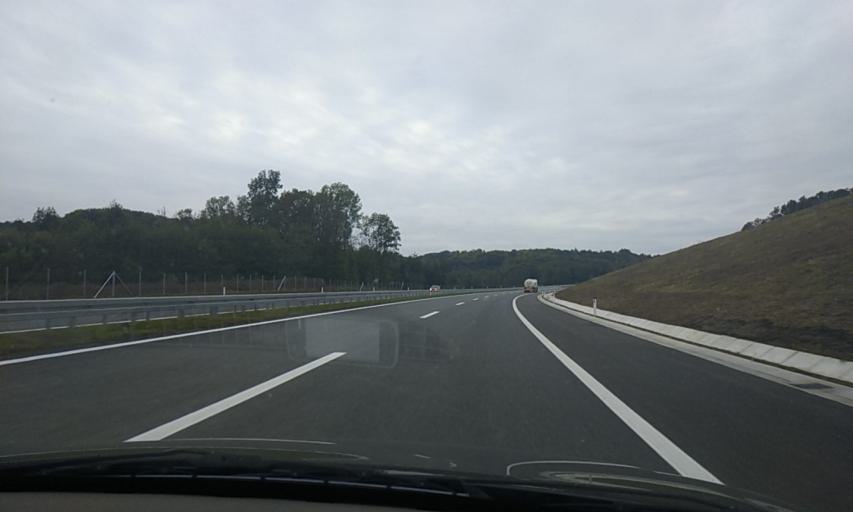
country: BA
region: Republika Srpska
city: Prnjavor
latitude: 44.8719
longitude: 17.5286
